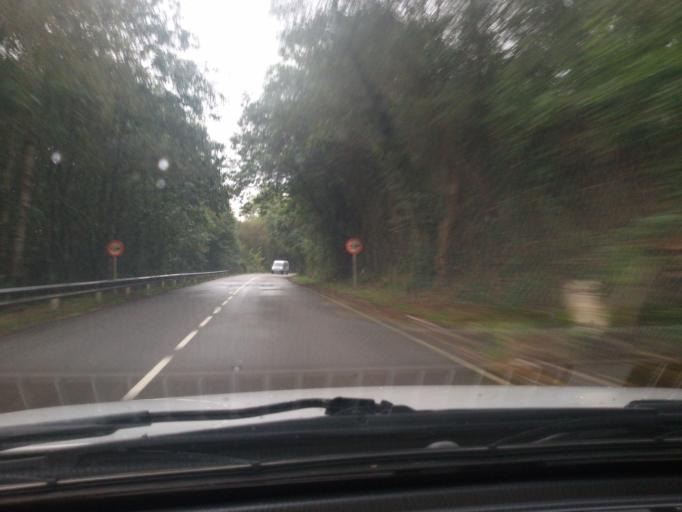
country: ES
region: Asturias
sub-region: Province of Asturias
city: Norena
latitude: 43.3742
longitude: -5.7171
